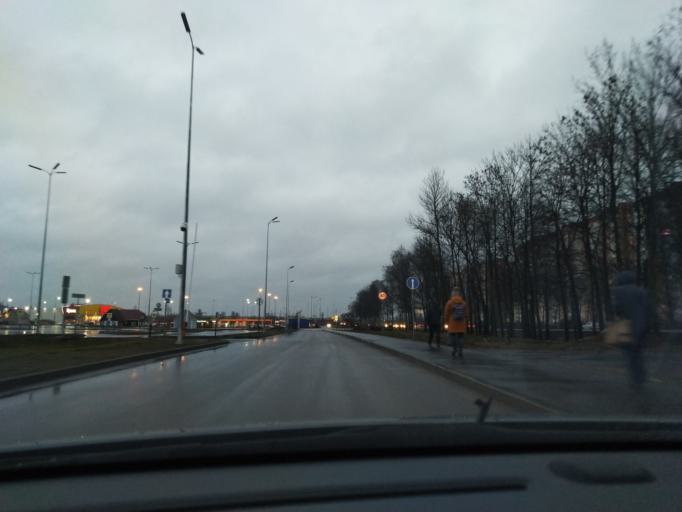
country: RU
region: St.-Petersburg
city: Gorelovo
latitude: 59.7922
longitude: 30.1467
